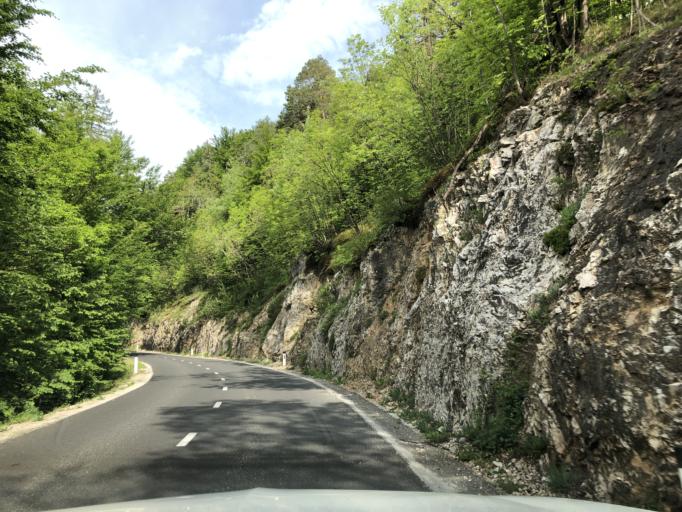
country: SI
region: Bloke
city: Nova Vas
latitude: 45.7981
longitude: 14.5608
